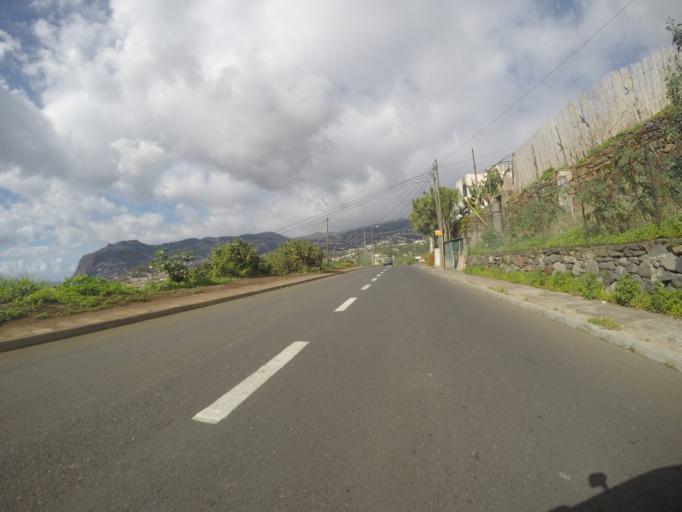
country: PT
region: Madeira
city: Camara de Lobos
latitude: 32.6475
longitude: -16.9577
